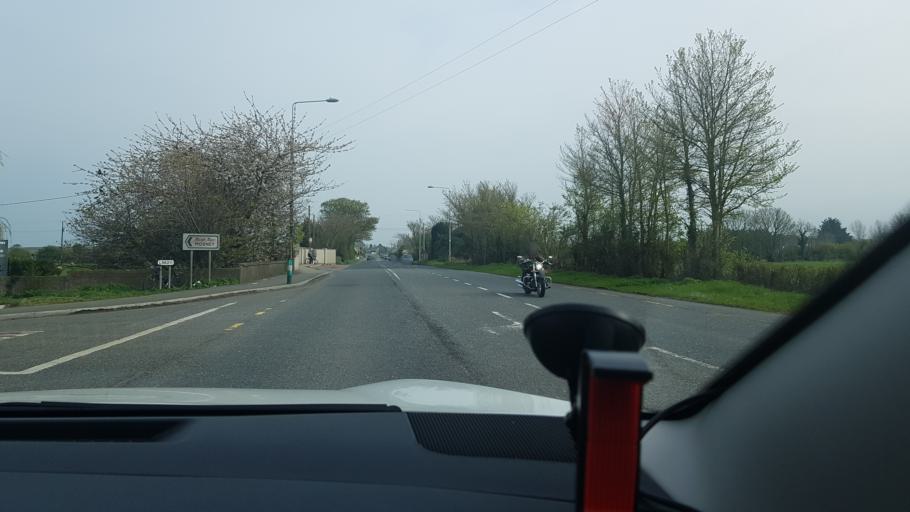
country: IE
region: Leinster
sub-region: An Mhi
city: Stamullin
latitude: 53.6580
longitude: -6.2631
